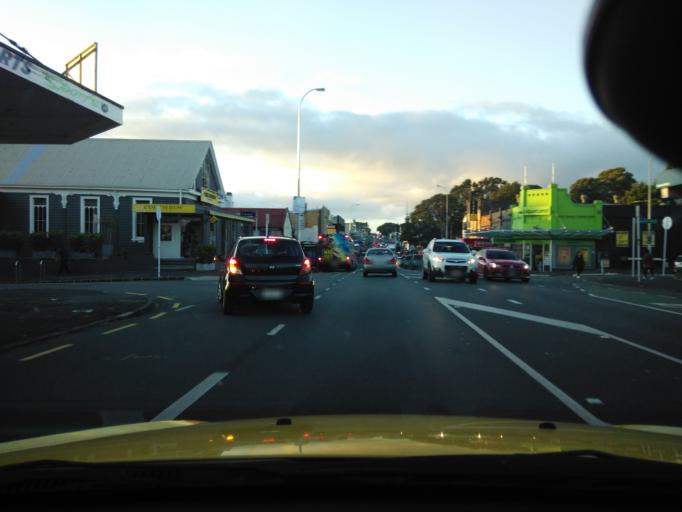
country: NZ
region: Auckland
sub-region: Auckland
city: Auckland
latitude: -36.8796
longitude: 174.7499
